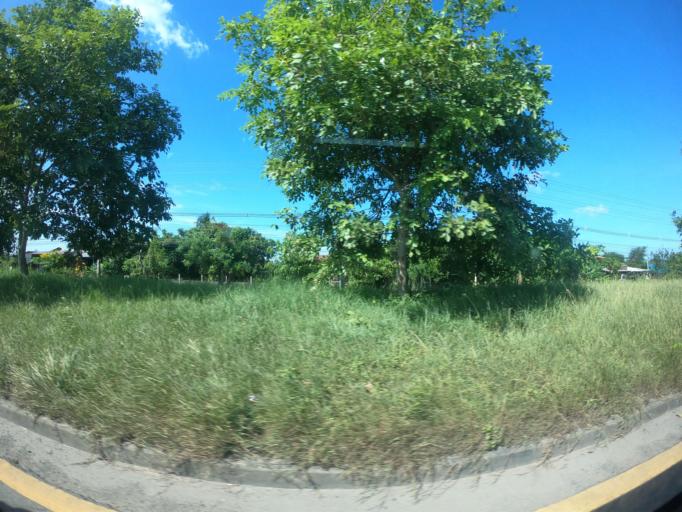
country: TH
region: Nakhon Nayok
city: Ban Na
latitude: 14.2502
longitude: 101.1003
